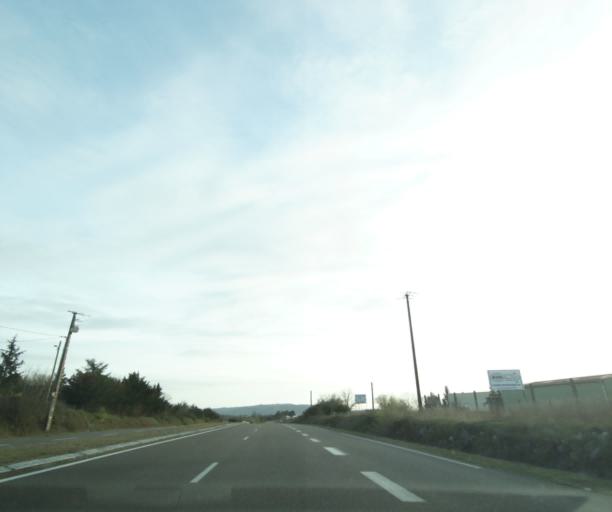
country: FR
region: Midi-Pyrenees
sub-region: Departement du Lot
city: Souillac
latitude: 44.9250
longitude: 1.4918
